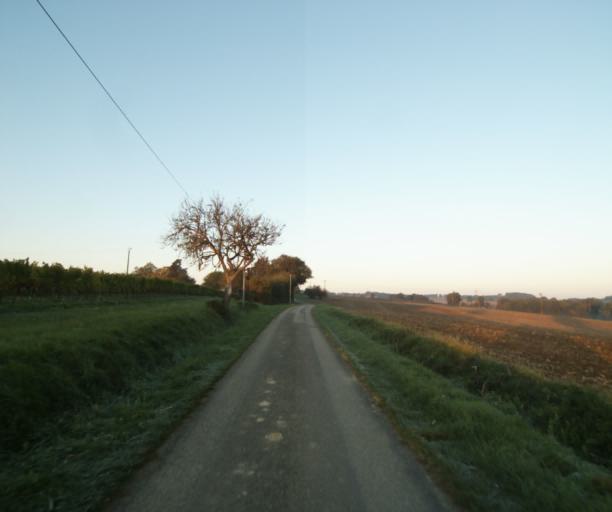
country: FR
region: Midi-Pyrenees
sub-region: Departement du Gers
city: Gondrin
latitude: 43.7931
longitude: 0.2122
